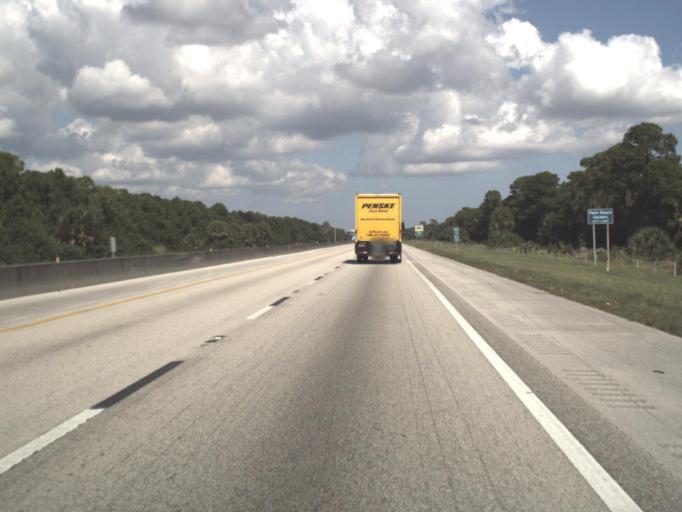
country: US
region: Florida
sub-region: Palm Beach County
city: Palm Beach Gardens
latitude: 26.7782
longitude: -80.1326
